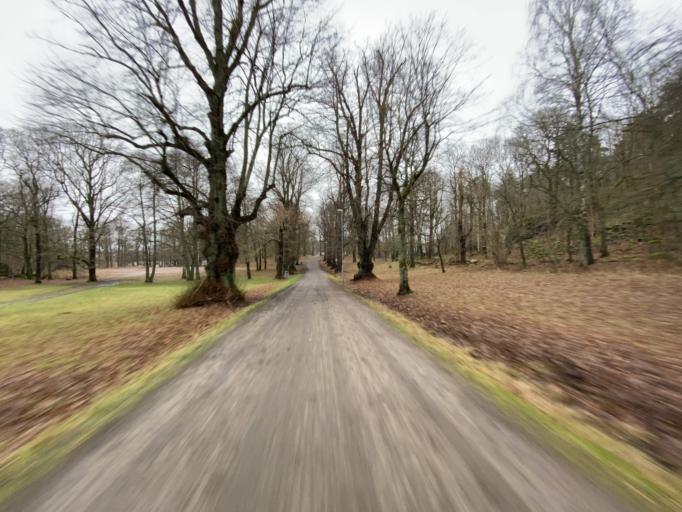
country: SE
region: Vaestra Goetaland
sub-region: Molndal
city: Moelndal
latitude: 57.7088
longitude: 12.0296
